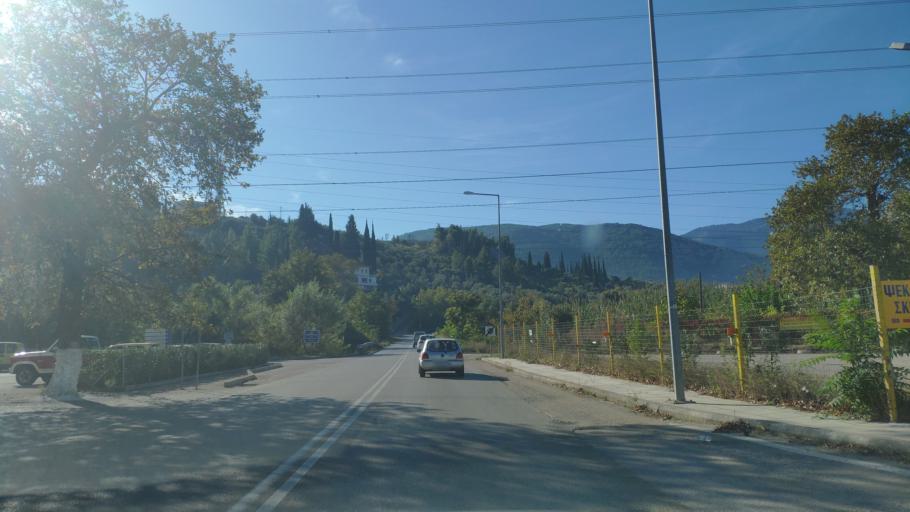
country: GR
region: Central Greece
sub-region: Nomos Voiotias
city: Livadeia
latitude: 38.4507
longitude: 22.8818
